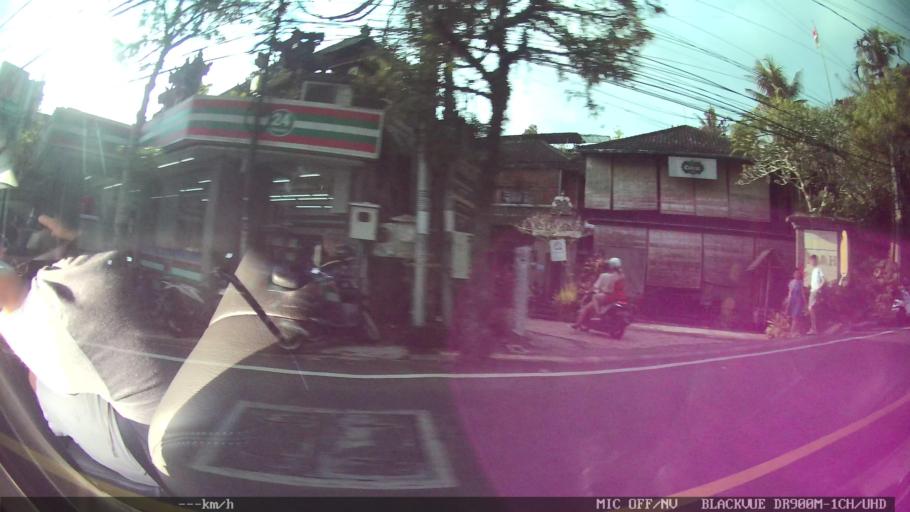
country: ID
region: Bali
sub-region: Kabupaten Gianyar
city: Ubud
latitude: -8.5052
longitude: 115.2563
